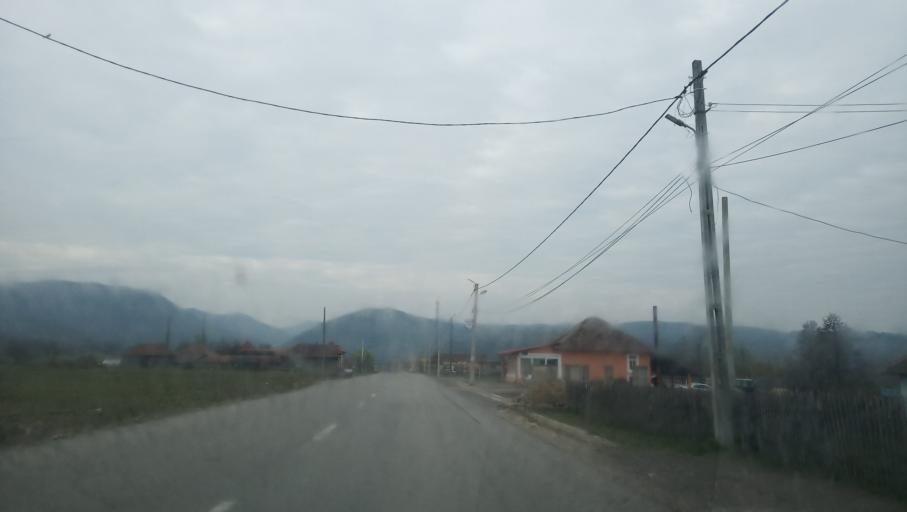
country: RO
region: Arad
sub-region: Comuna Varfurile
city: Varfurile
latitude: 46.3130
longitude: 22.5348
